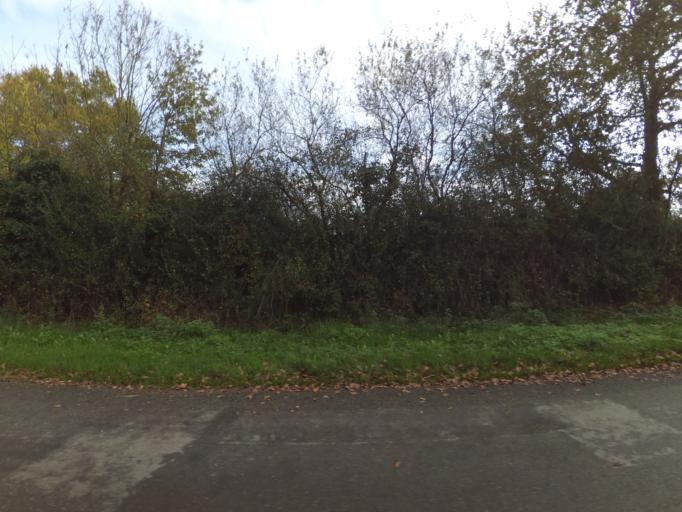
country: FR
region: Pays de la Loire
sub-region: Departement de la Vendee
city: Saint-Hilaire-de-Loulay
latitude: 47.0295
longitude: -1.3463
